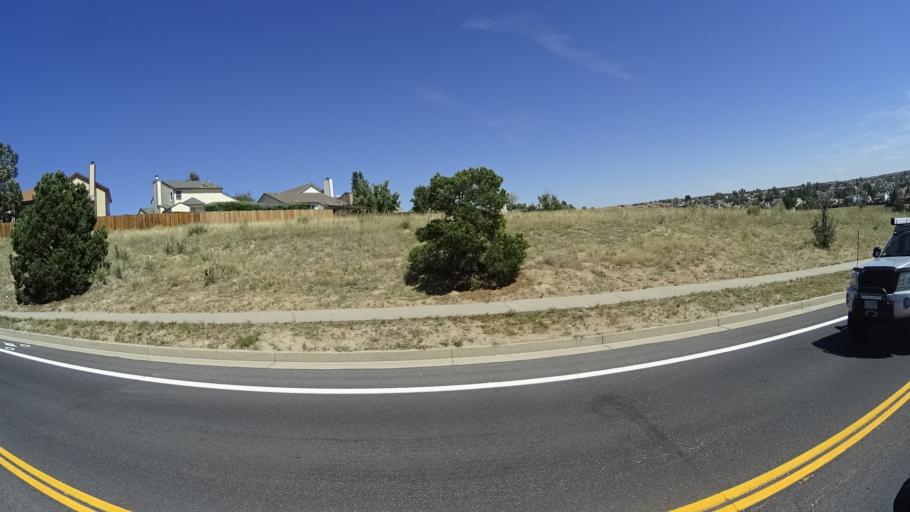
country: US
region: Colorado
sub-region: El Paso County
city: Black Forest
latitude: 38.9476
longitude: -104.7462
